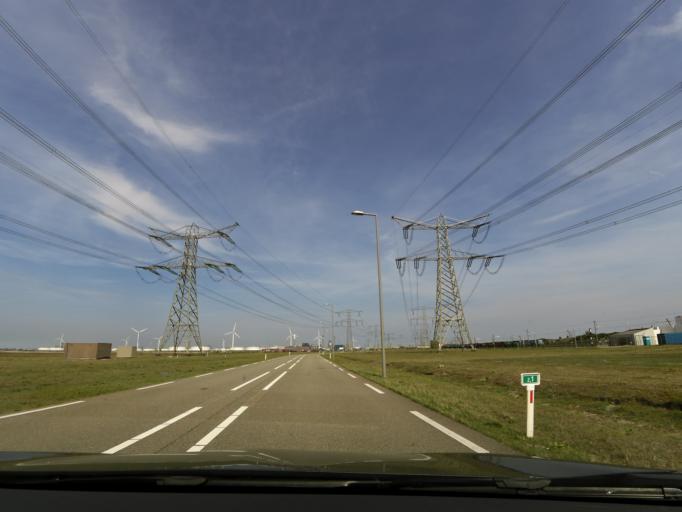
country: NL
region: South Holland
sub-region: Gemeente Rotterdam
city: Hoek van Holland
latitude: 51.9344
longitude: 4.0679
